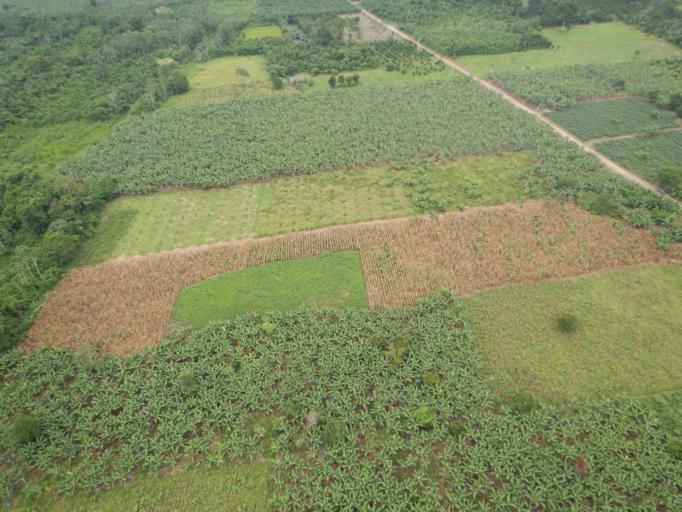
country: BO
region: Cochabamba
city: Chimore
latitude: -17.1418
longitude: -64.8073
